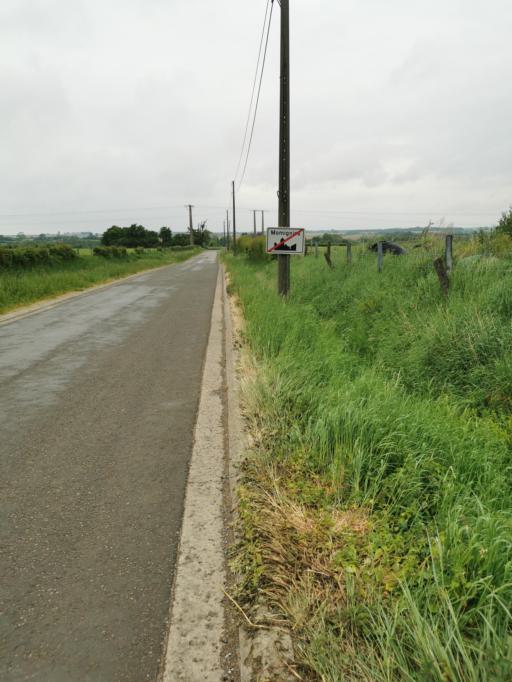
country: BE
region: Wallonia
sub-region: Province du Hainaut
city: Momignies
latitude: 50.0346
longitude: 4.1619
